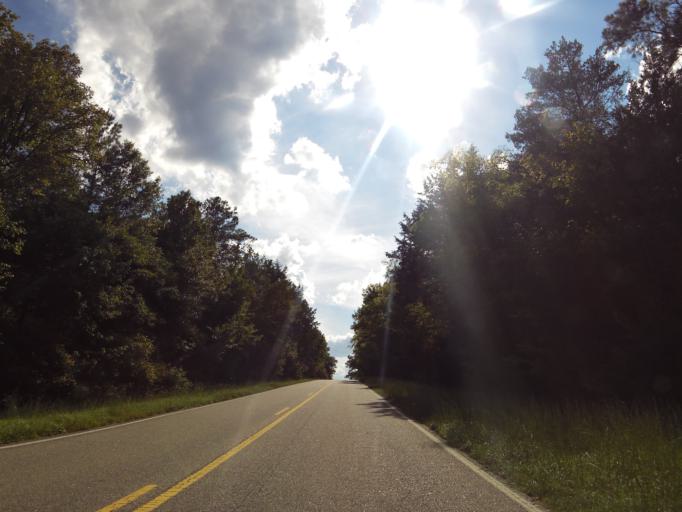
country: US
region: Alabama
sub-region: Dallas County
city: Selmont-West Selmont
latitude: 32.1881
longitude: -87.0355
